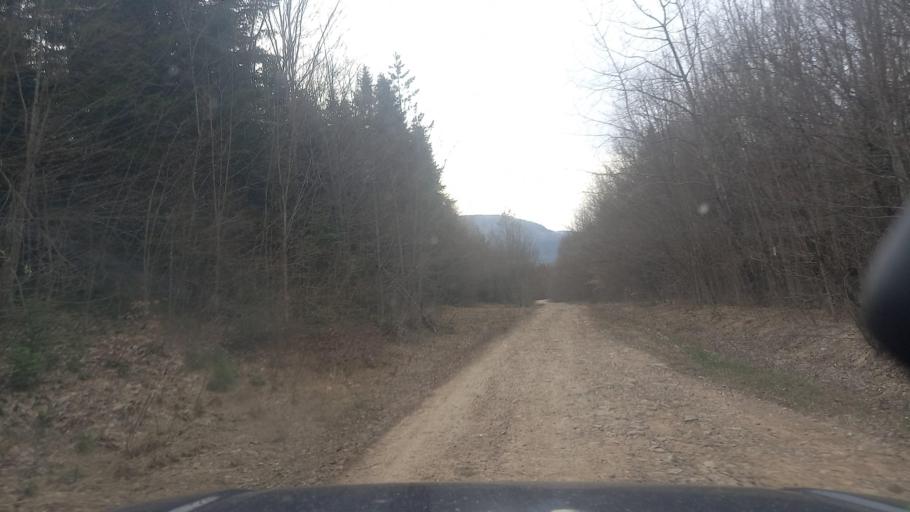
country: RU
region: Adygeya
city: Kamennomostskiy
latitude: 44.1860
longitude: 39.9883
